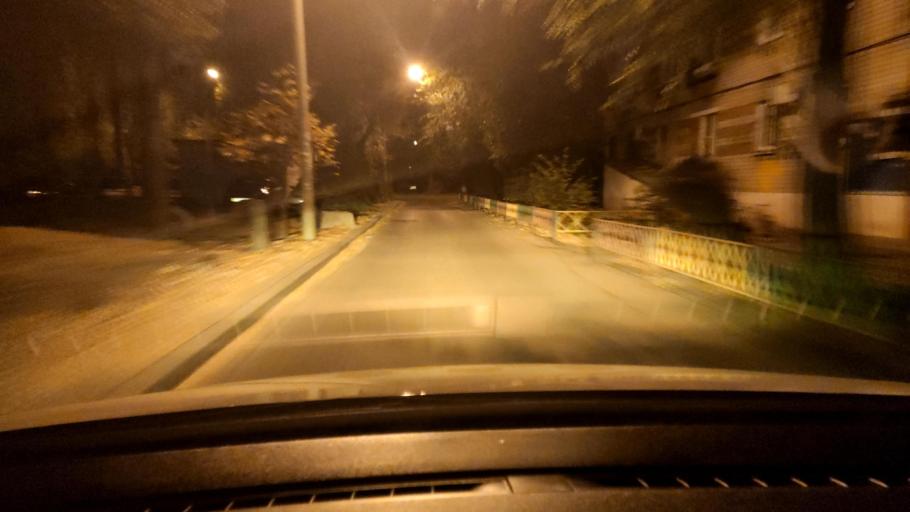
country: RU
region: Voronezj
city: Voronezh
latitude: 51.6484
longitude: 39.1468
